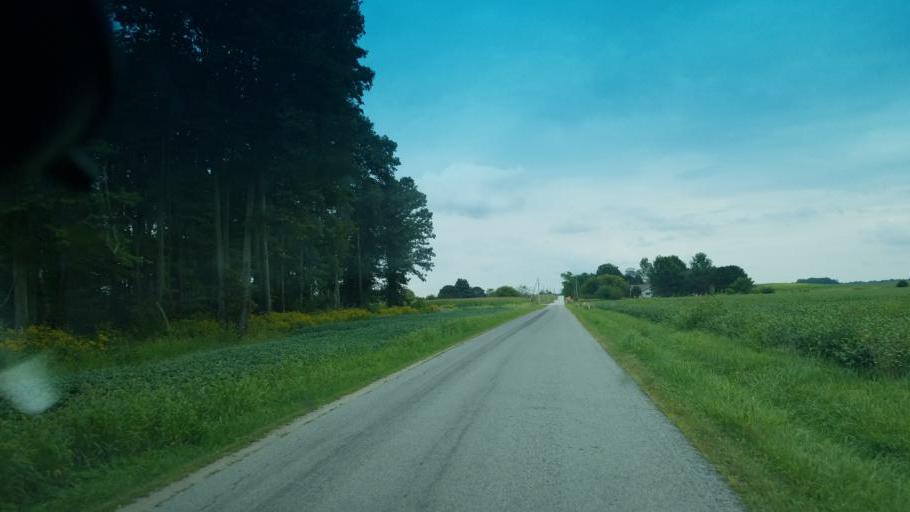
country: US
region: Ohio
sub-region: Richland County
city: Shelby
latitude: 40.8939
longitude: -82.7277
